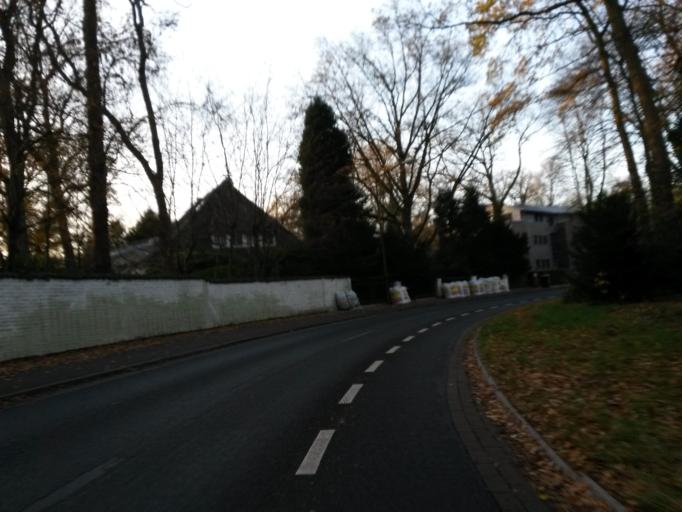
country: DE
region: Lower Saxony
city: Lilienthal
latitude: 53.0894
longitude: 8.8902
